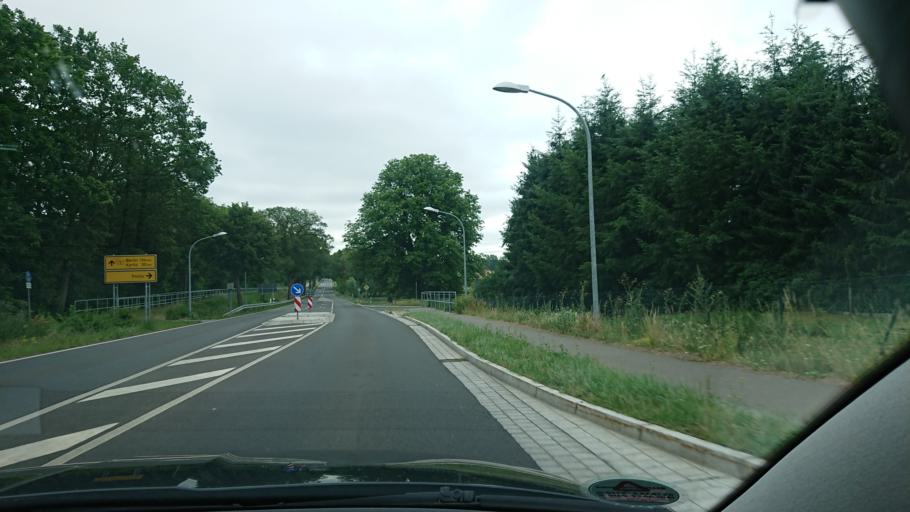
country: DE
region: Brandenburg
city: Bad Wilsnack
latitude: 53.0313
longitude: 11.9711
